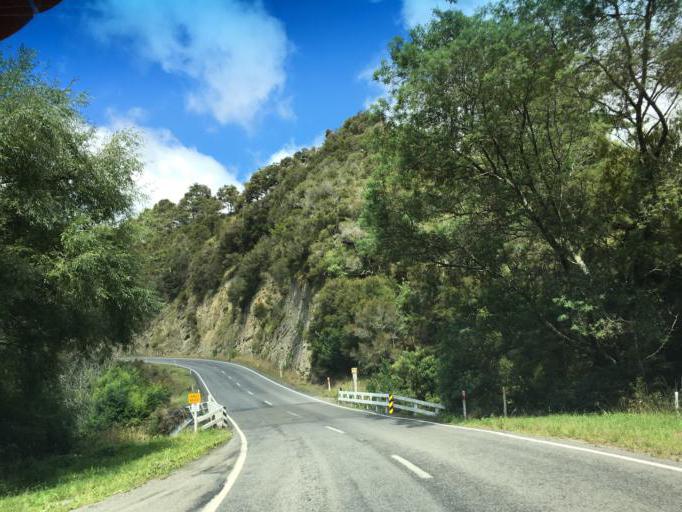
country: NZ
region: Hawke's Bay
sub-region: Napier City
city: Napier
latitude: -39.1293
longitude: 176.9972
